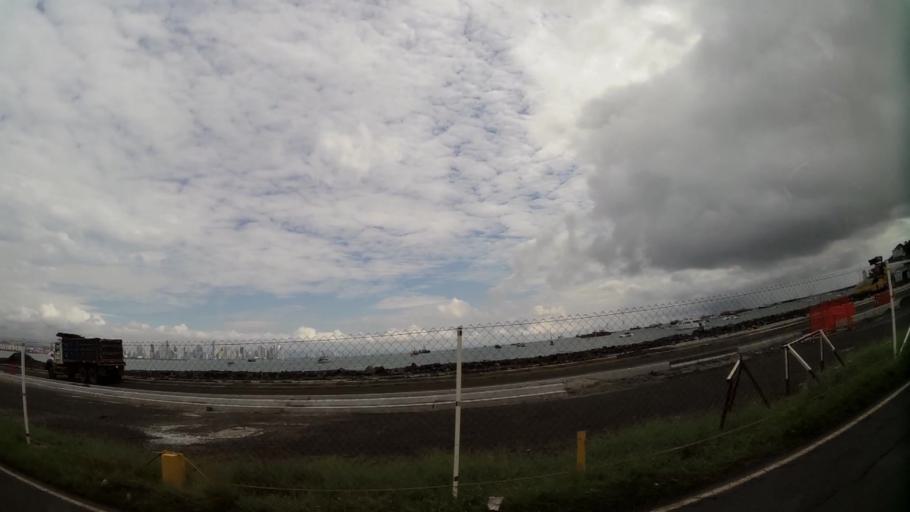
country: PA
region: Panama
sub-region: Distrito de Panama
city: Ancon
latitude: 8.9195
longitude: -79.5354
